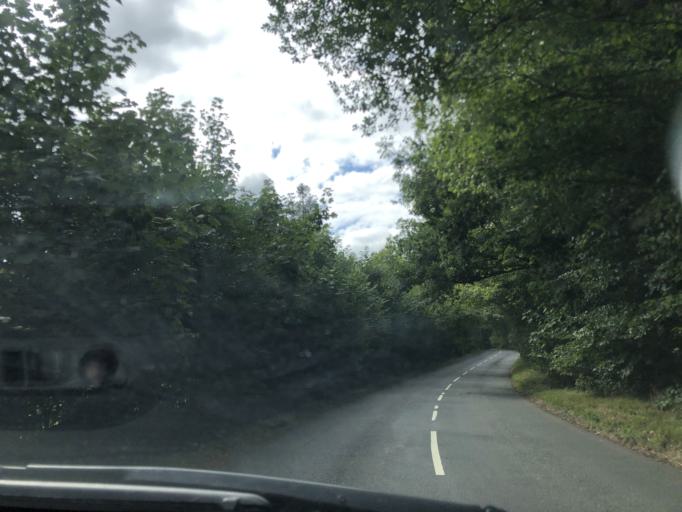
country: GB
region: England
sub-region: East Sussex
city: Forest Row
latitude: 51.0807
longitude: 0.0710
